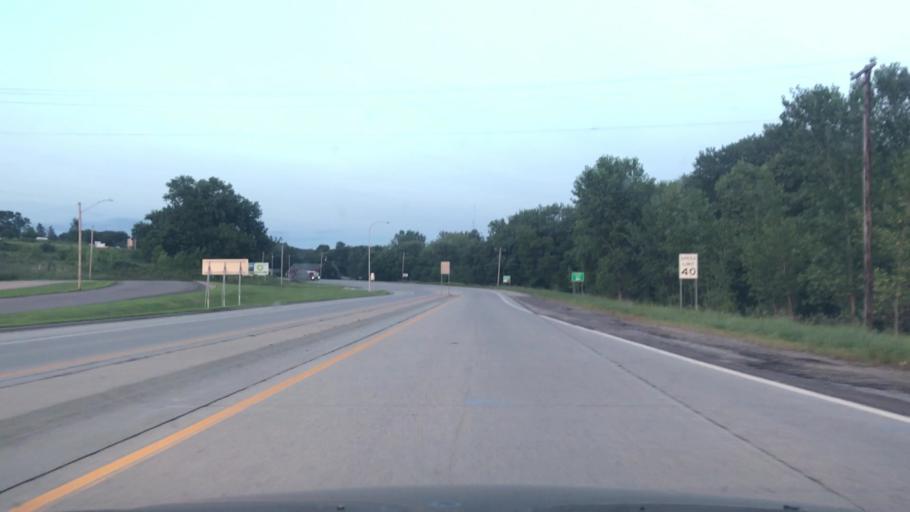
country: US
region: Minnesota
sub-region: Redwood County
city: Redwood Falls
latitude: 44.5491
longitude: -94.9923
